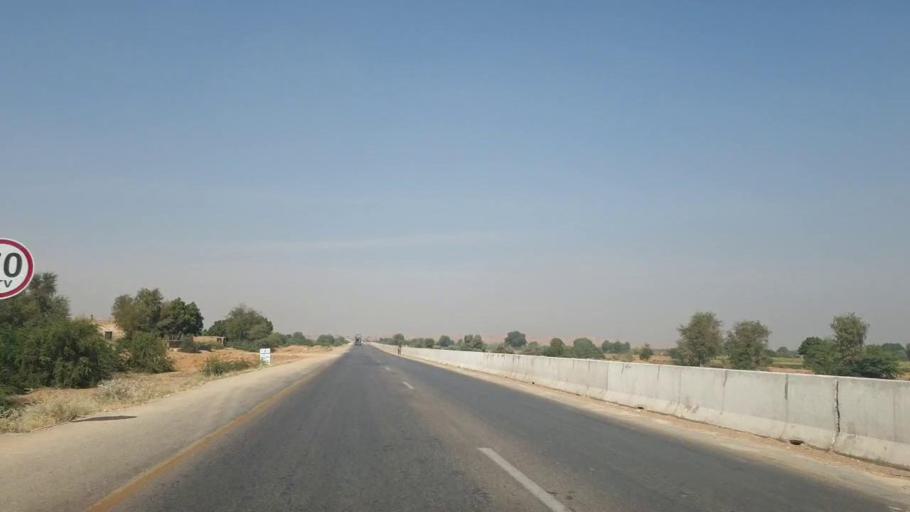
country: PK
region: Sindh
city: Matiari
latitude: 25.5954
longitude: 68.3084
